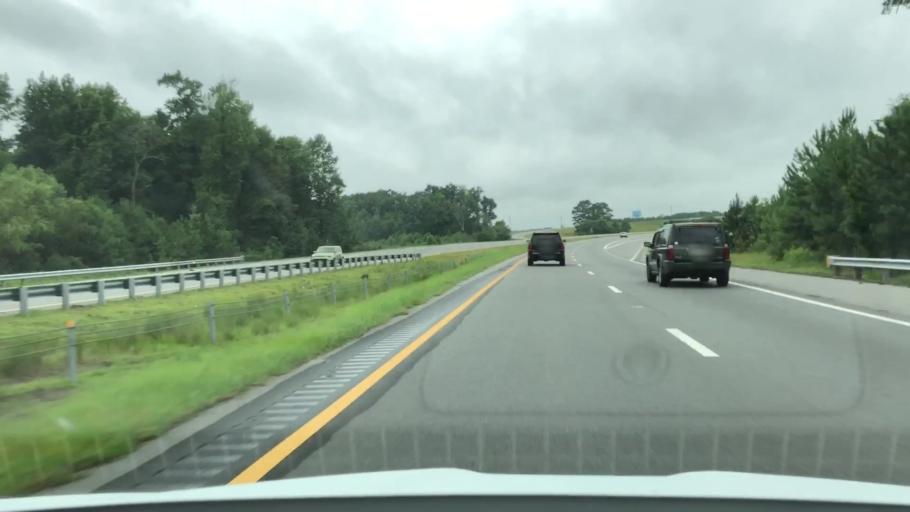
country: US
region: North Carolina
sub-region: Wayne County
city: Goldsboro
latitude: 35.4179
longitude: -77.9284
